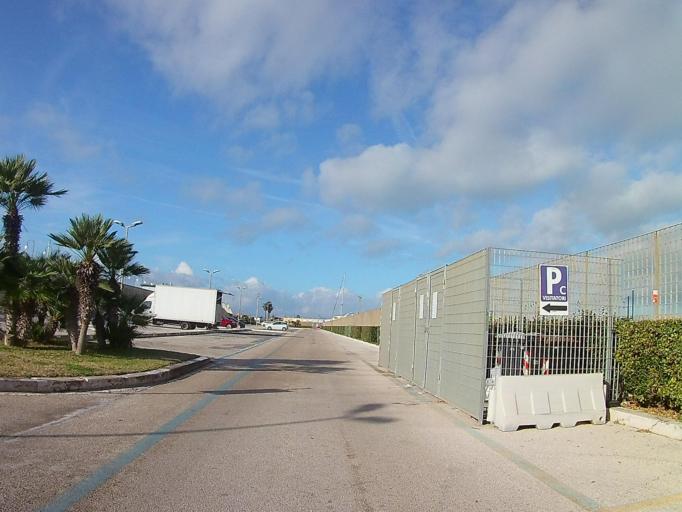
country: IT
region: Latium
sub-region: Citta metropolitana di Roma Capitale
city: Lido di Ostia
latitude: 41.7395
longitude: 12.2452
